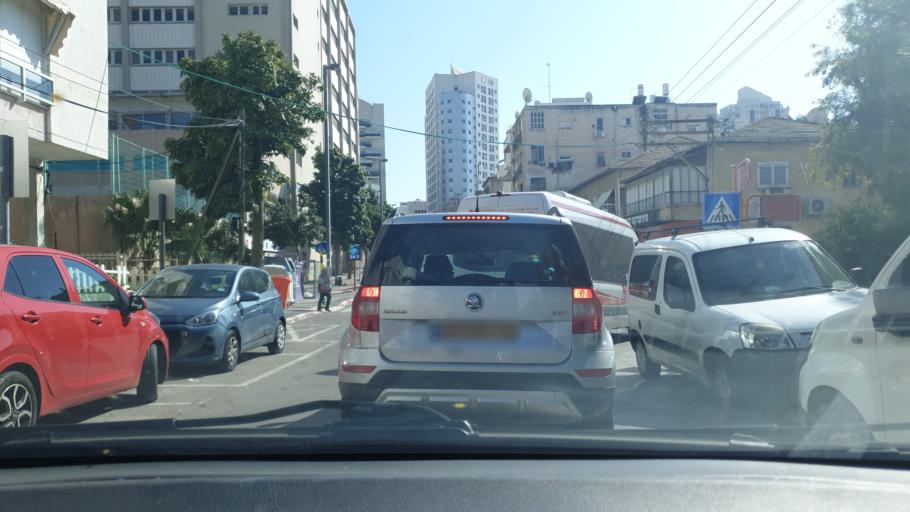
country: IL
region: Central District
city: Rishon LeZiyyon
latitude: 31.9698
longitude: 34.8035
